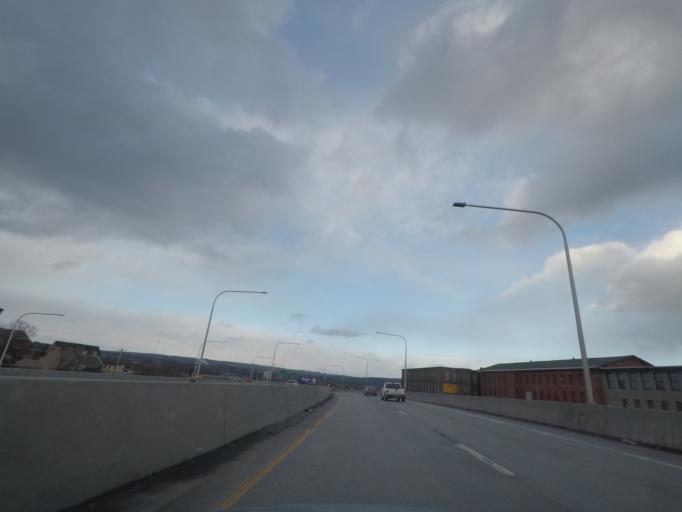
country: US
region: New York
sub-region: Oneida County
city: Utica
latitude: 43.1021
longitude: -75.2406
